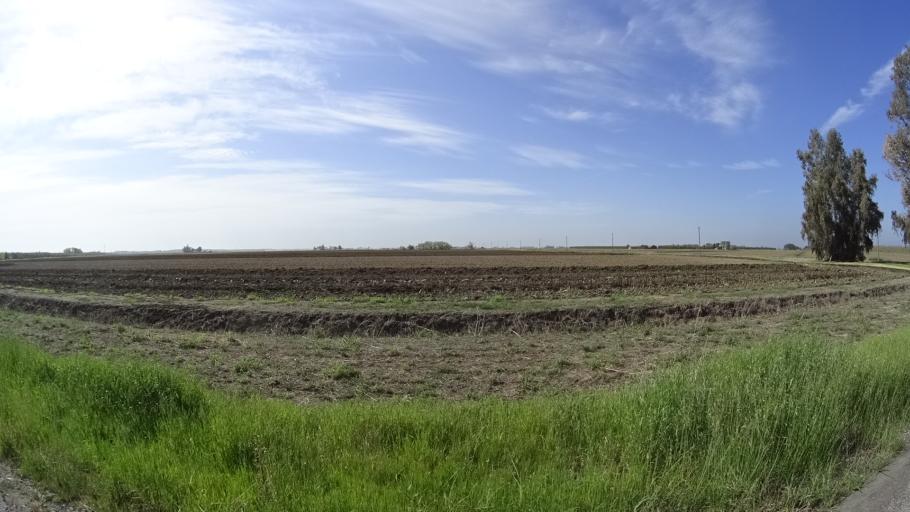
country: US
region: California
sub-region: Glenn County
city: Hamilton City
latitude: 39.6234
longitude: -122.0359
